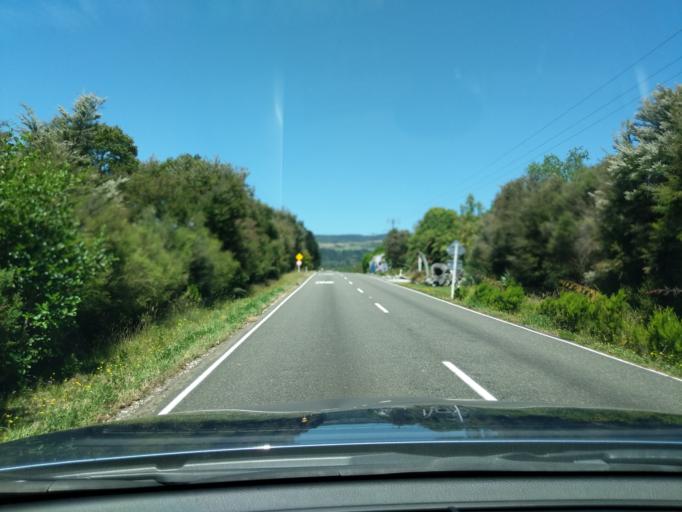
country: NZ
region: Tasman
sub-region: Tasman District
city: Takaka
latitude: -40.7262
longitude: 172.6067
